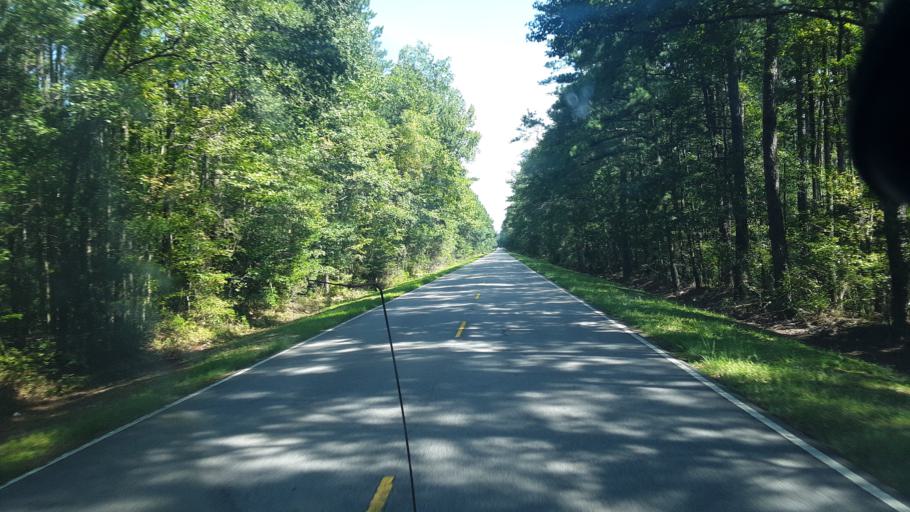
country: US
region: South Carolina
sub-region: Hampton County
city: Hampton
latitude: 33.0051
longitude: -81.0469
